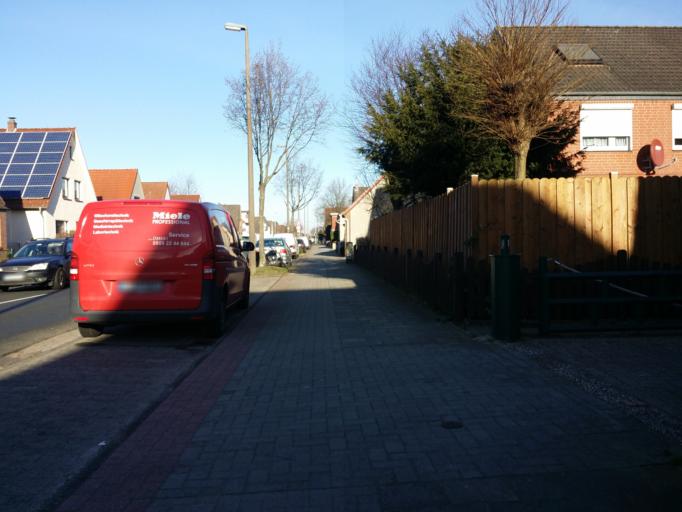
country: DE
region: Lower Saxony
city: Delmenhorst
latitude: 53.0409
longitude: 8.6533
